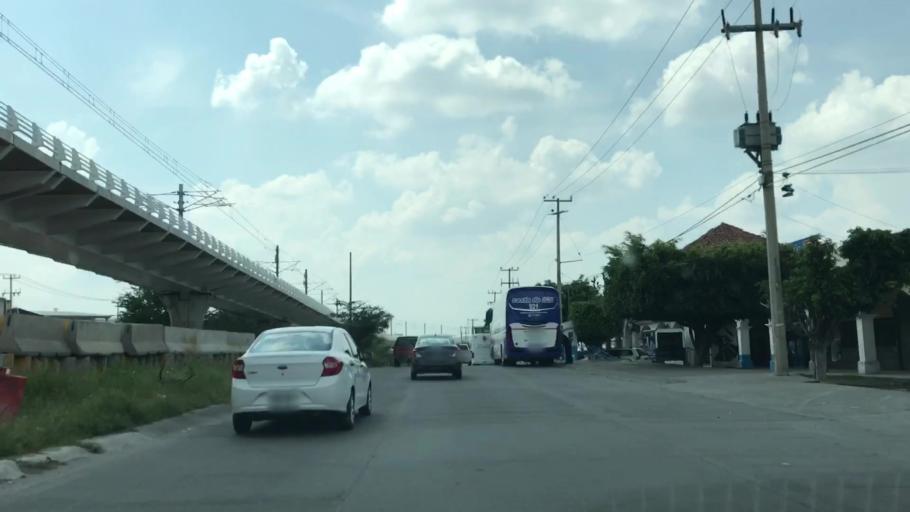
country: MX
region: Jalisco
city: Tlaquepaque
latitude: 20.6244
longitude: -103.2881
